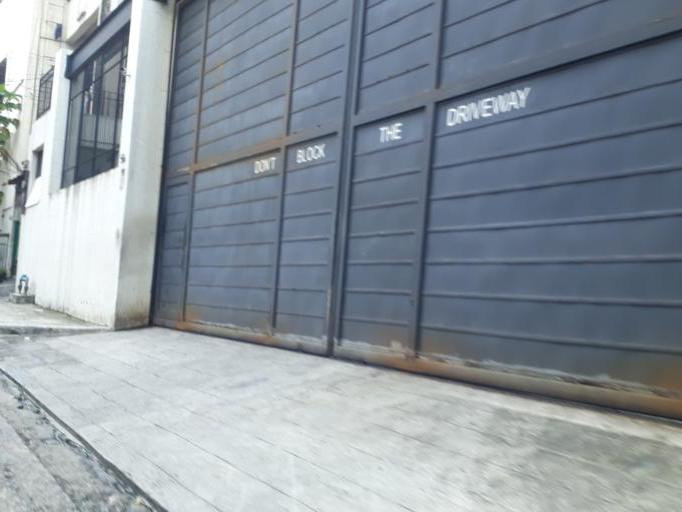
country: PH
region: Metro Manila
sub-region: San Juan
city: San Juan
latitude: 14.6160
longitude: 121.0489
